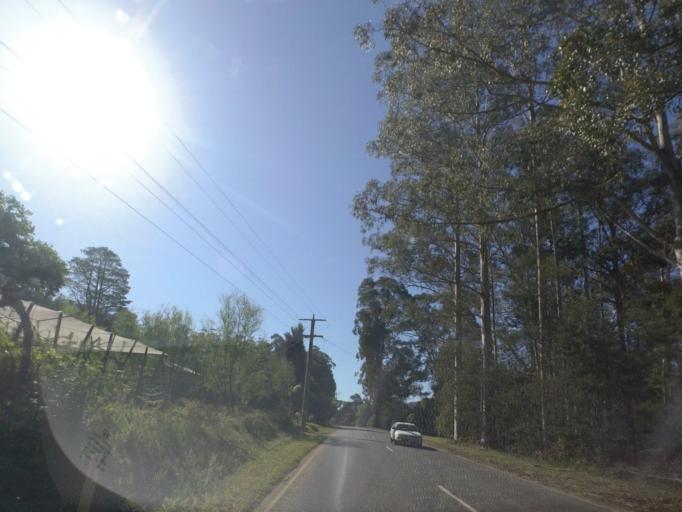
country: AU
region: Victoria
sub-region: Yarra Ranges
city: Millgrove
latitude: -37.8473
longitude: 145.6876
